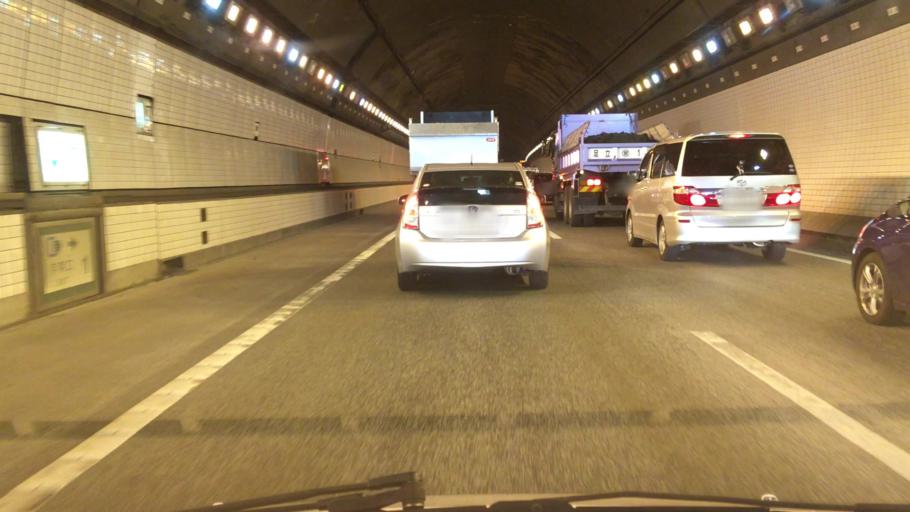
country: JP
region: Kanagawa
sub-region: Kawasaki-shi
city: Kawasaki
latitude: 35.5262
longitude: 139.7944
